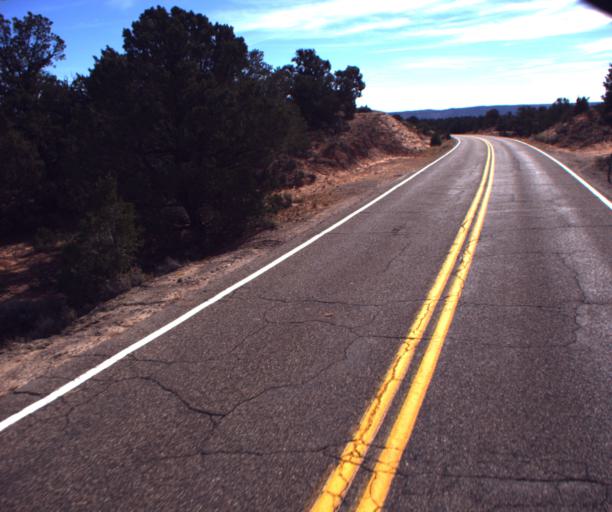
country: US
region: Arizona
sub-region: Navajo County
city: Kayenta
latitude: 36.6462
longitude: -110.5174
